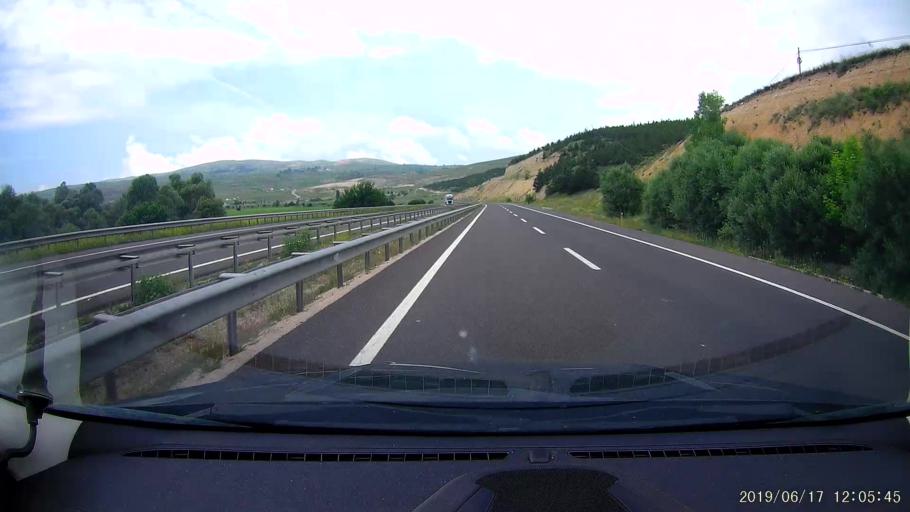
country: TR
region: Cankiri
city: Cerkes
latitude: 40.8356
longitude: 32.7729
